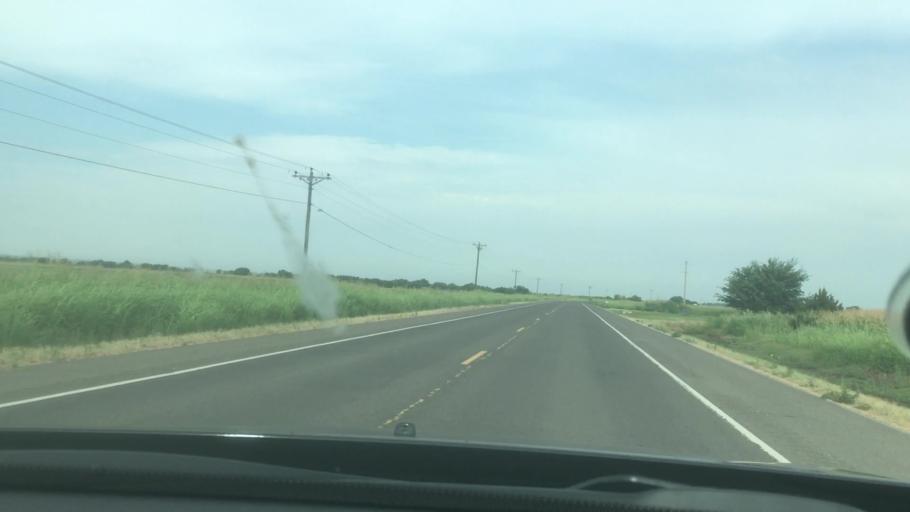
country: US
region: Oklahoma
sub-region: Garvin County
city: Maysville
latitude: 34.8192
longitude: -97.4824
